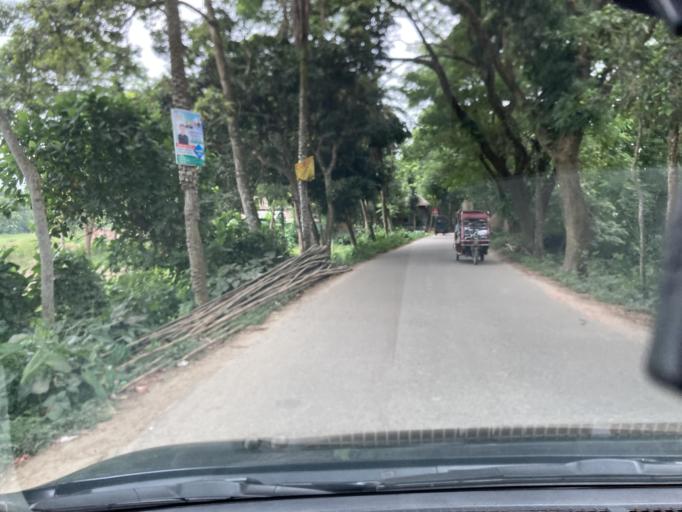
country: BD
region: Dhaka
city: Dohar
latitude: 23.7973
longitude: 90.0488
